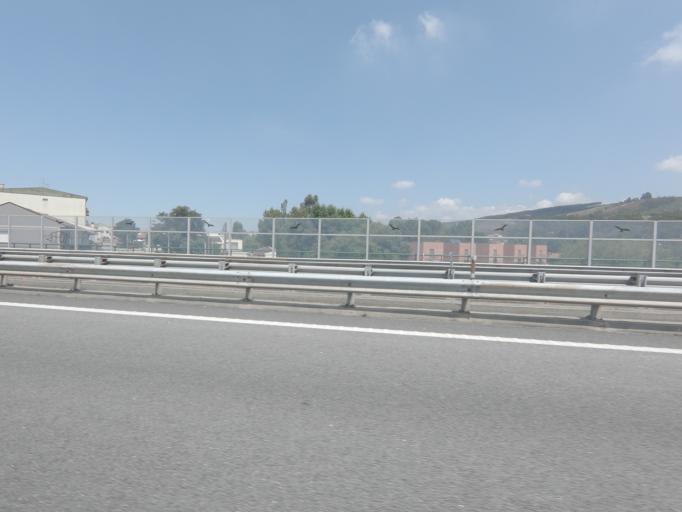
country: PT
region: Porto
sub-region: Valongo
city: Valongo
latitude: 41.1969
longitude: -8.4981
